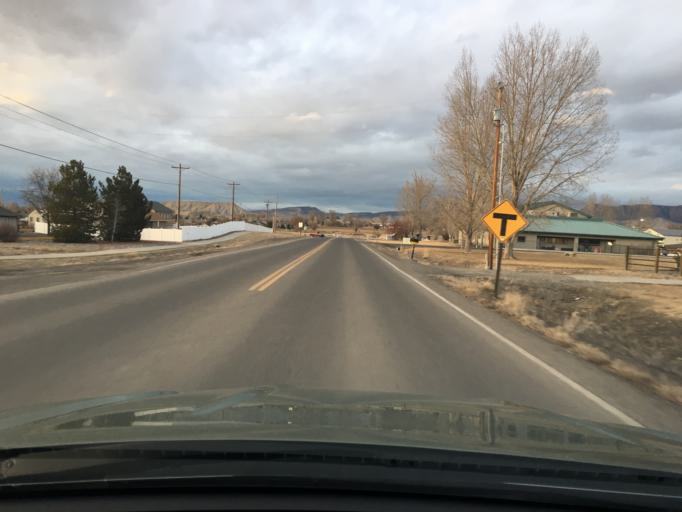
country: US
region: Colorado
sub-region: Montrose County
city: Montrose
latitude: 38.4728
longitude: -107.8387
